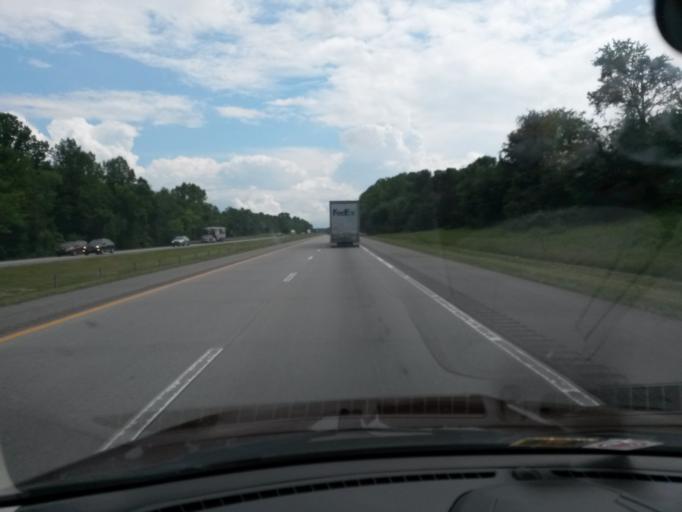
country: US
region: North Carolina
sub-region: Yadkin County
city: Jonesville
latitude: 36.1332
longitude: -80.8111
